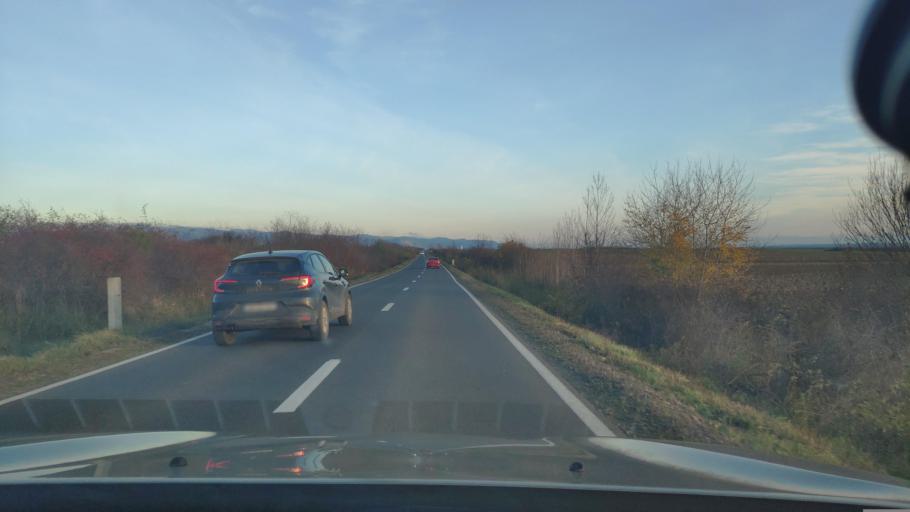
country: RO
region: Satu Mare
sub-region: Comuna Mediesu Aurit
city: Mediesu Aurit
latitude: 47.7708
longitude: 23.1424
